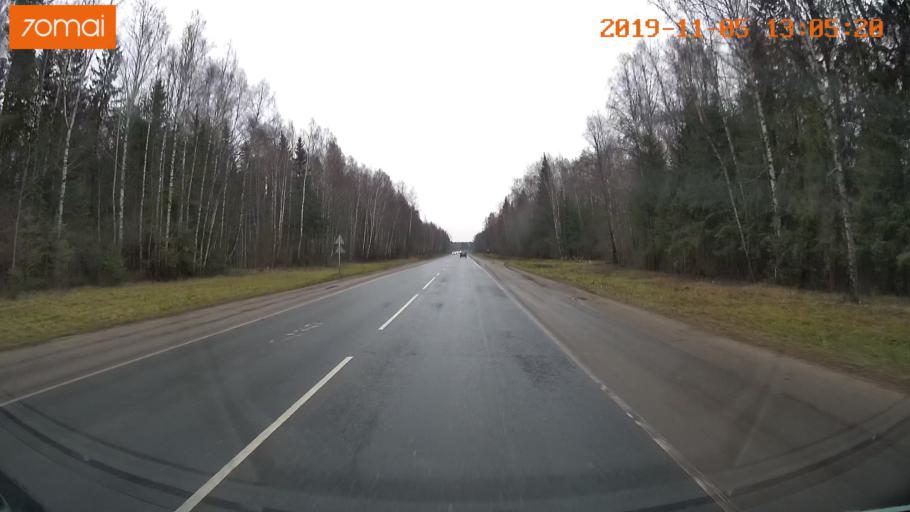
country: RU
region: Ivanovo
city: Kitovo
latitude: 56.8832
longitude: 41.2407
